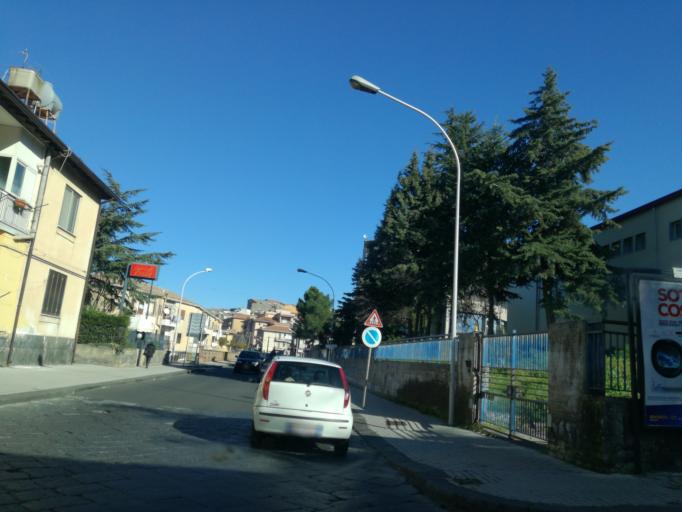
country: IT
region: Sicily
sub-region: Catania
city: Bronte
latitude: 37.7830
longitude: 14.8360
